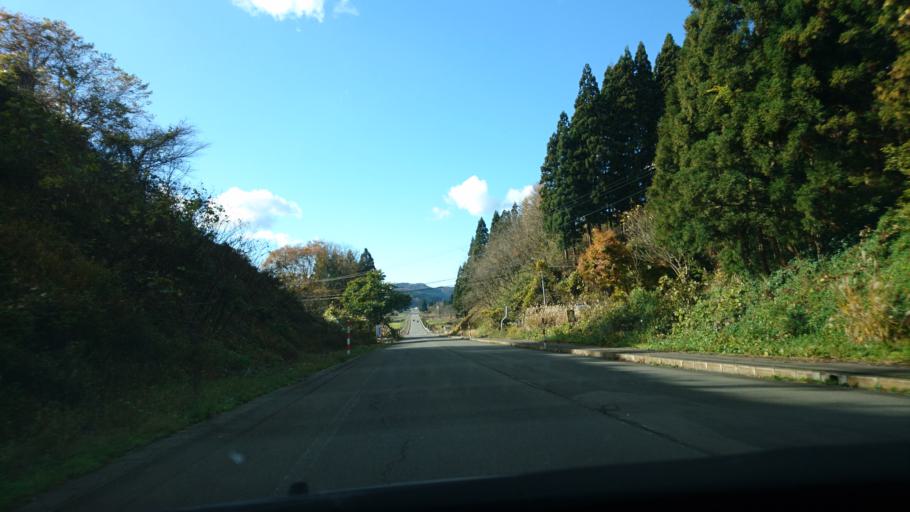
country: JP
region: Akita
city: Omagari
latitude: 39.3073
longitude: 140.2467
